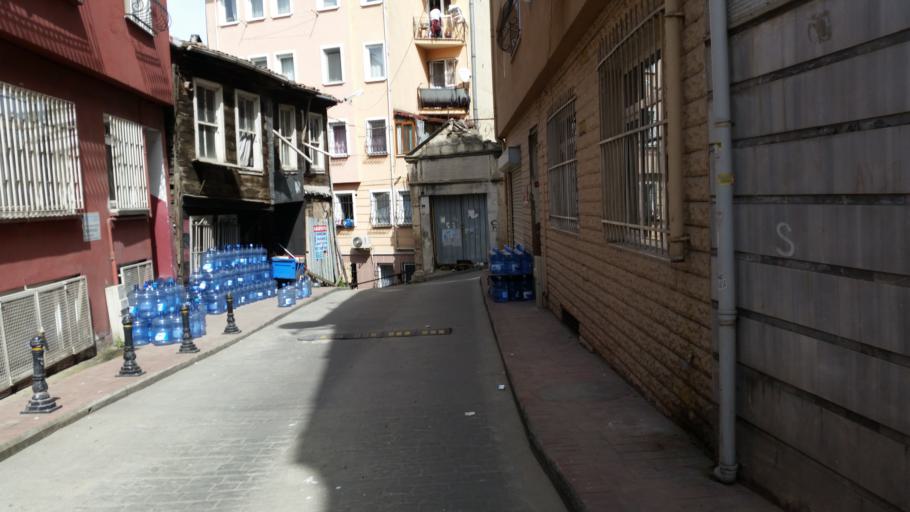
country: TR
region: Istanbul
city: Eminoenue
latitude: 41.0356
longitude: 28.9711
